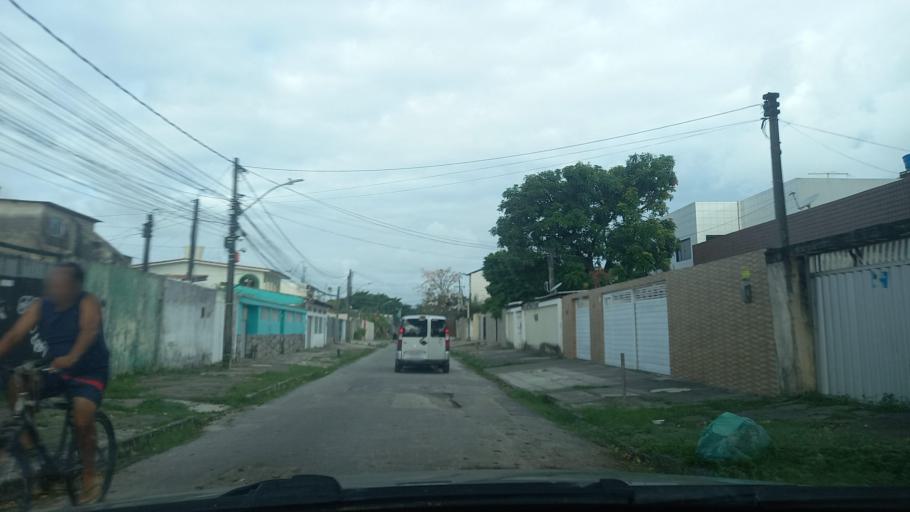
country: BR
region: Pernambuco
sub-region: Recife
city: Recife
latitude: -8.1118
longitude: -34.9181
